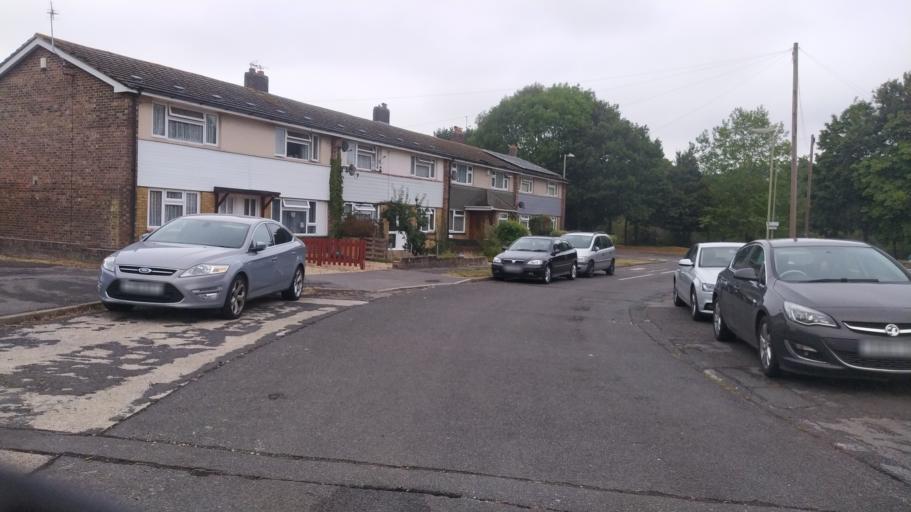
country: GB
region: England
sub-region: Hampshire
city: Havant
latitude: 50.8682
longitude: -0.9664
